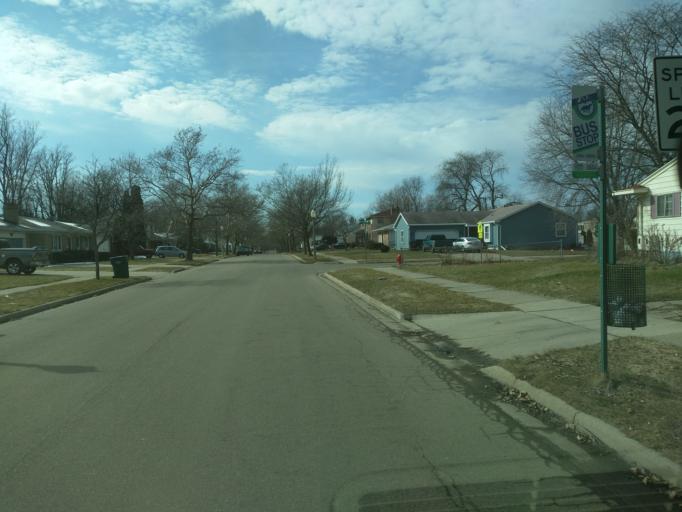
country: US
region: Michigan
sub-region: Ingham County
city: Lansing
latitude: 42.7052
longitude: -84.5830
